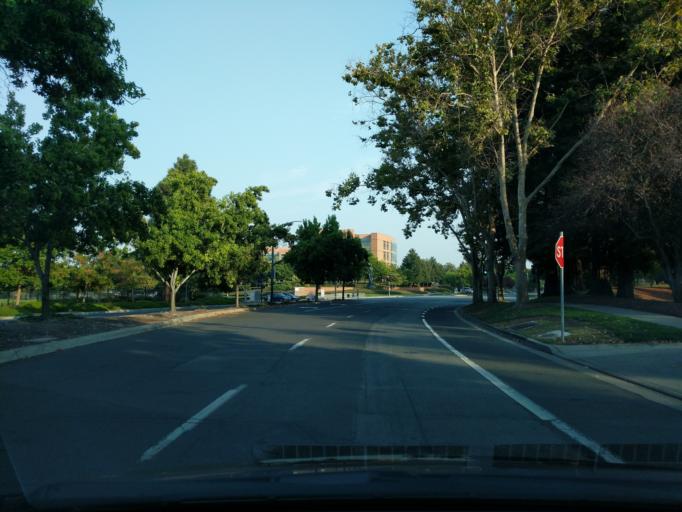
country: US
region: California
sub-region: Santa Clara County
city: Mountain View
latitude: 37.4244
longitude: -122.0908
